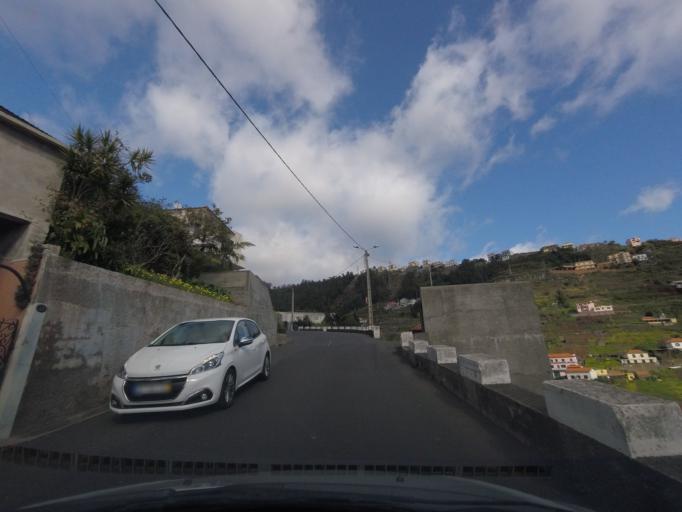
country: PT
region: Madeira
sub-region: Ribeira Brava
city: Campanario
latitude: 32.6639
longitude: -17.0085
